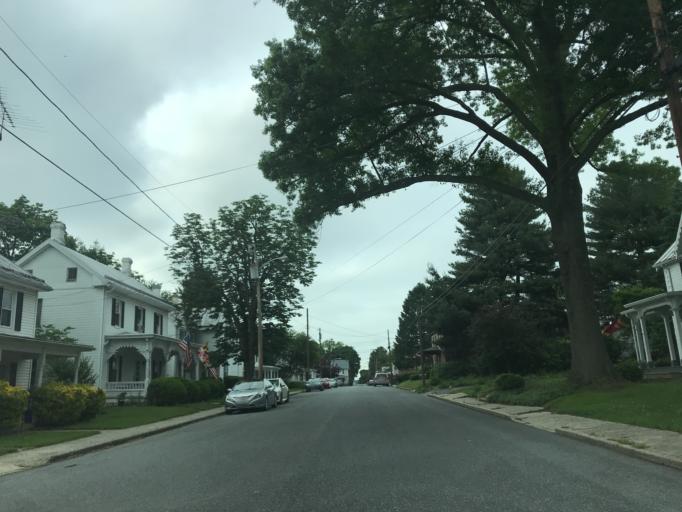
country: US
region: Maryland
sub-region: Frederick County
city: Walkersville
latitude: 39.4849
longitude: -77.3502
